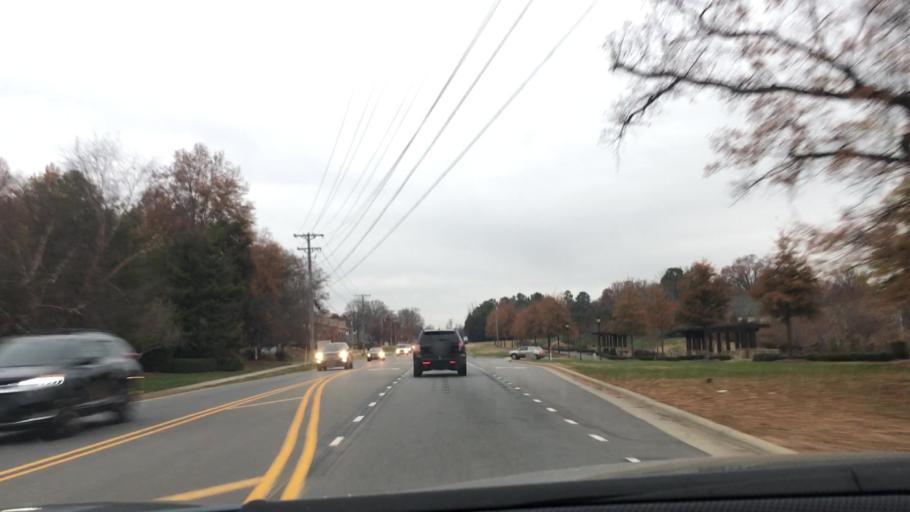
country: US
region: North Carolina
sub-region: Mecklenburg County
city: Cornelius
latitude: 35.4574
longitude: -80.8885
